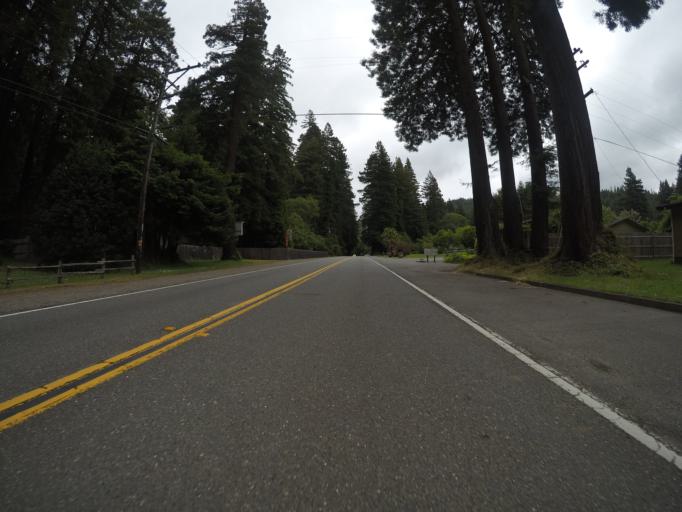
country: US
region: California
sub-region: Humboldt County
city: Rio Dell
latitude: 40.4004
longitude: -123.9494
